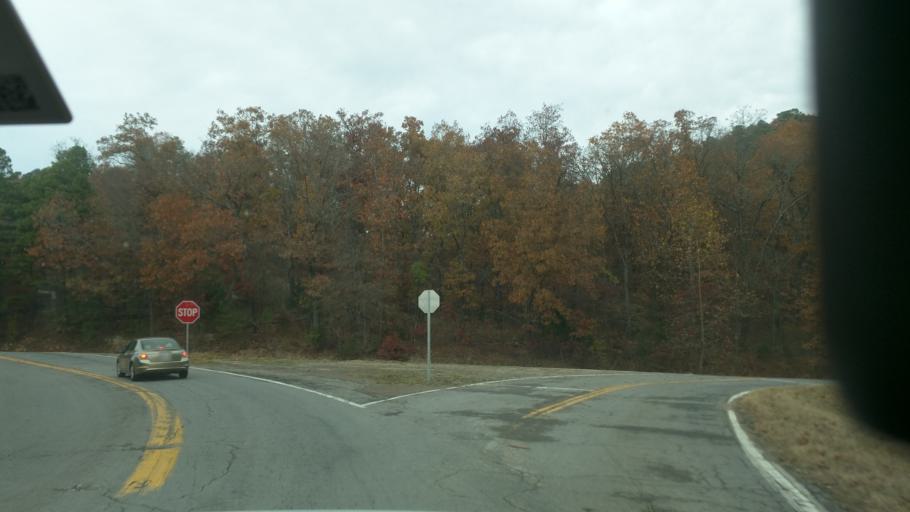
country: US
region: Oklahoma
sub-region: Cherokee County
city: Tahlequah
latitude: 35.9276
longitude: -94.8399
